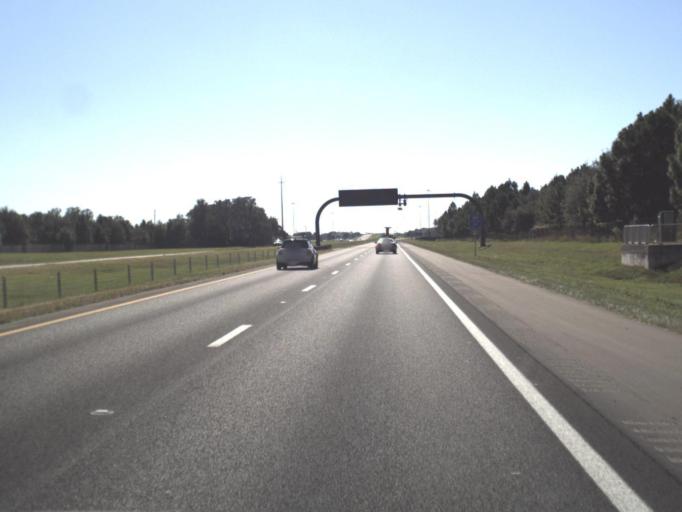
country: US
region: Florida
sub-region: Hernando County
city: Masaryktown
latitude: 28.4475
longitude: -82.4853
